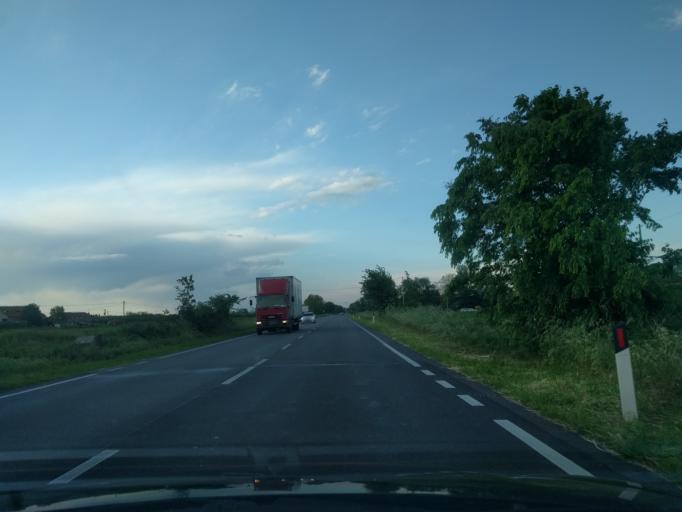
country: IT
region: Veneto
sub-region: Provincia di Rovigo
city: Polesella
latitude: 44.9456
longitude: 11.7350
